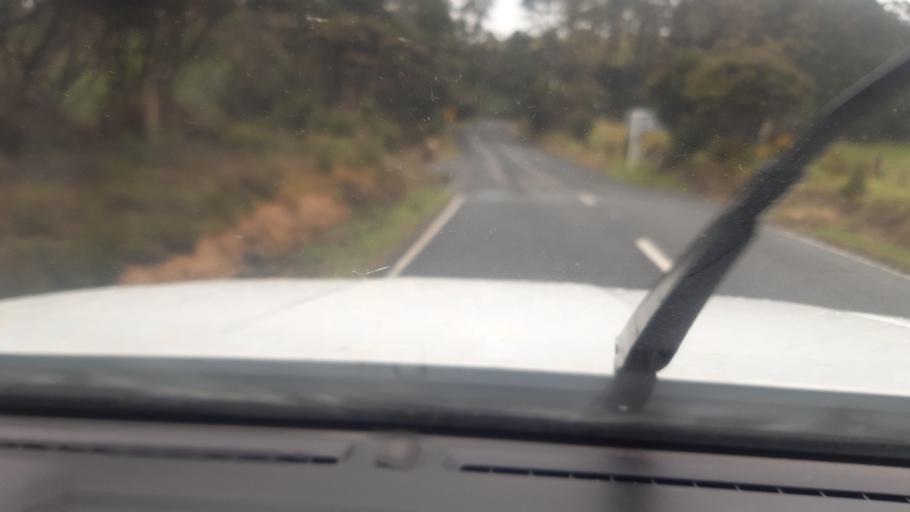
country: NZ
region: Northland
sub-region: Far North District
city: Kaitaia
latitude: -34.9999
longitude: 173.2156
